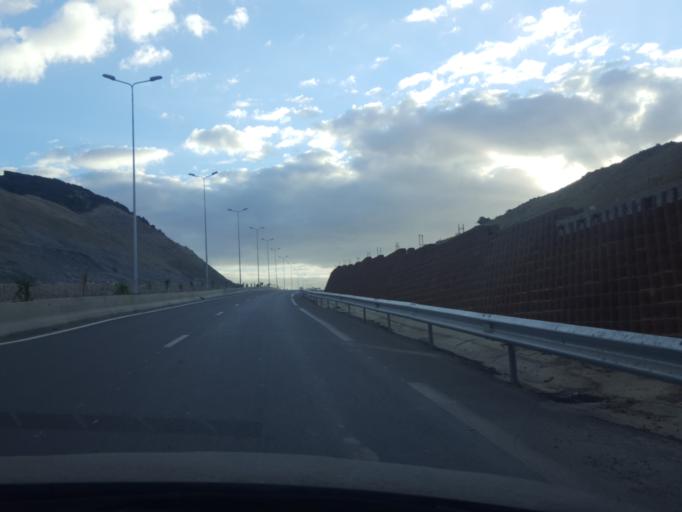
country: TN
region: Tunis
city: Hammam-Lif
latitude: 36.6948
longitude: 10.3980
